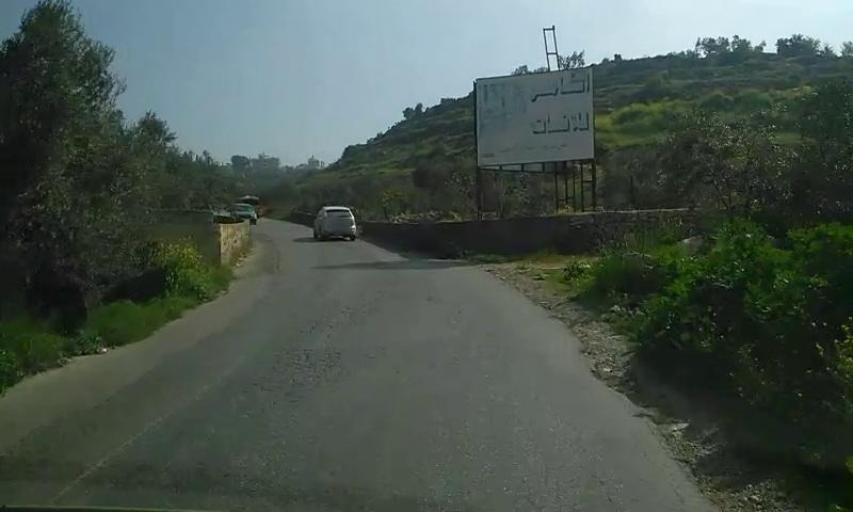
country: PS
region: West Bank
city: `Ayn Yabrud
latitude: 31.9512
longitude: 35.2431
